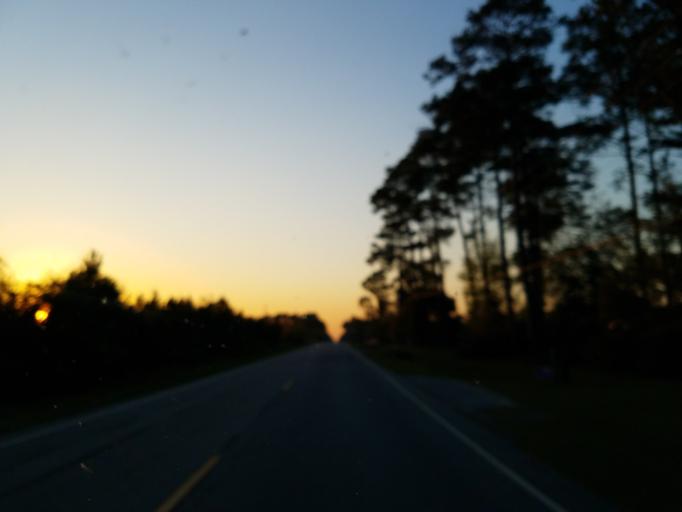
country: US
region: Georgia
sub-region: Berrien County
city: Ray City
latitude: 31.0590
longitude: -83.1526
